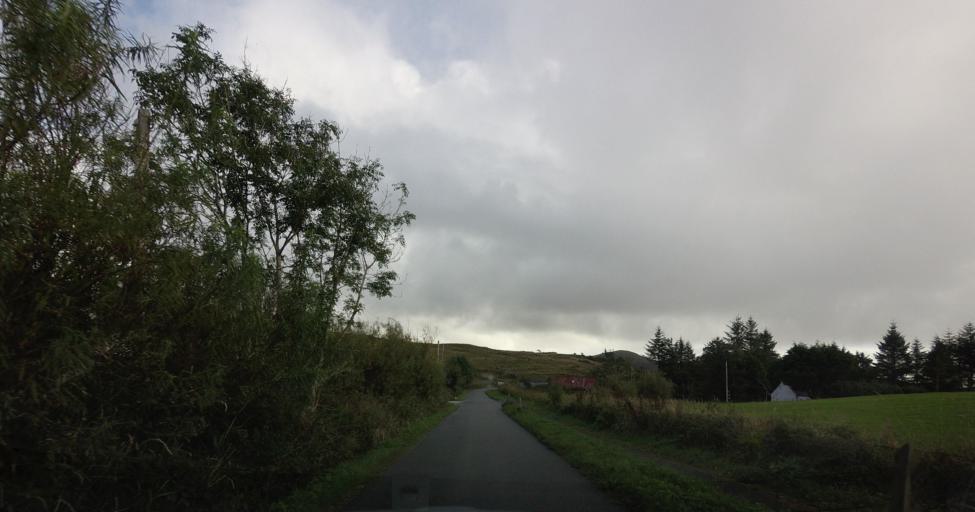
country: GB
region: Scotland
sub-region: Highland
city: Portree
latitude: 57.2128
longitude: -6.0097
